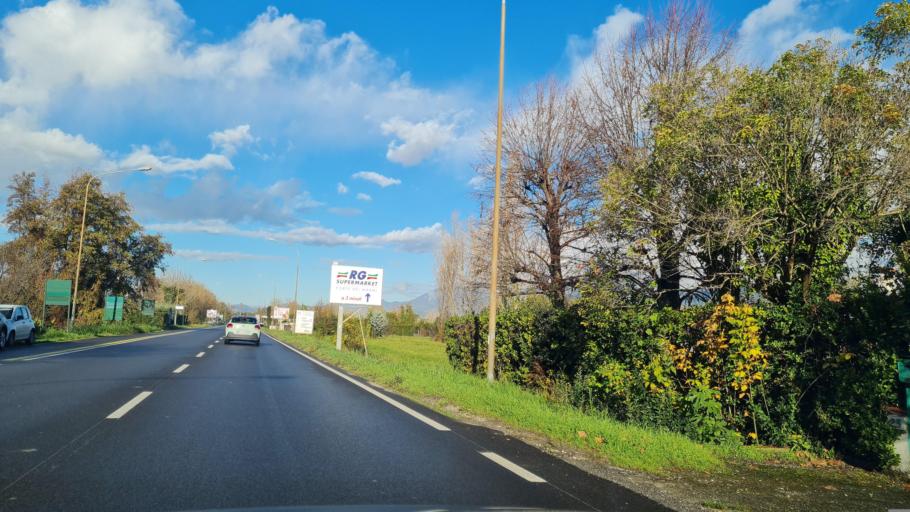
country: IT
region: Tuscany
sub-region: Provincia di Lucca
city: Pietrasanta
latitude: 43.9485
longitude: 10.2046
